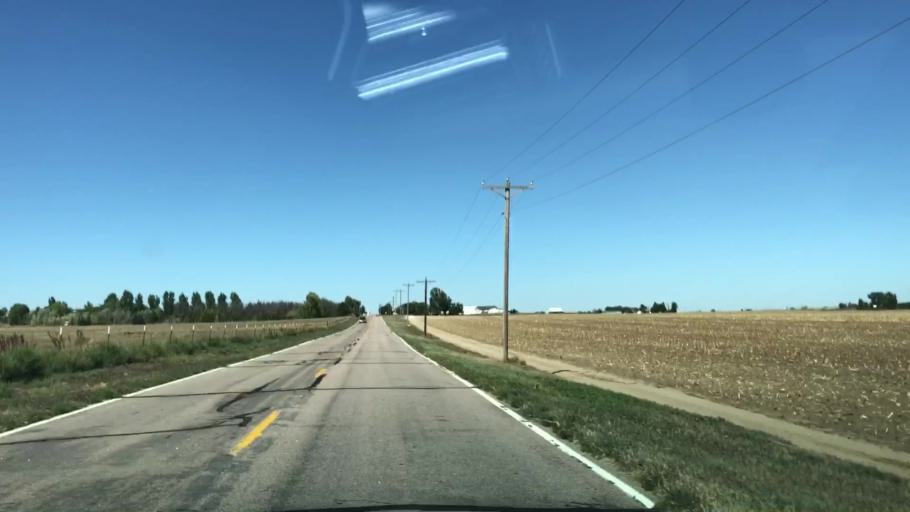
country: US
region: Colorado
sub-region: Weld County
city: Windsor
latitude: 40.5261
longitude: -104.9270
